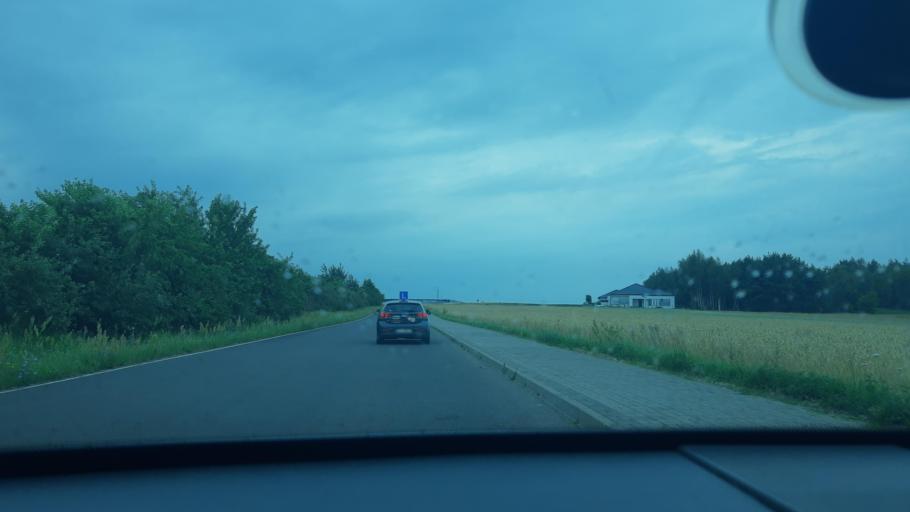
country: PL
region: Lodz Voivodeship
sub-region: Powiat sieradzki
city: Sieradz
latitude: 51.5774
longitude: 18.7035
